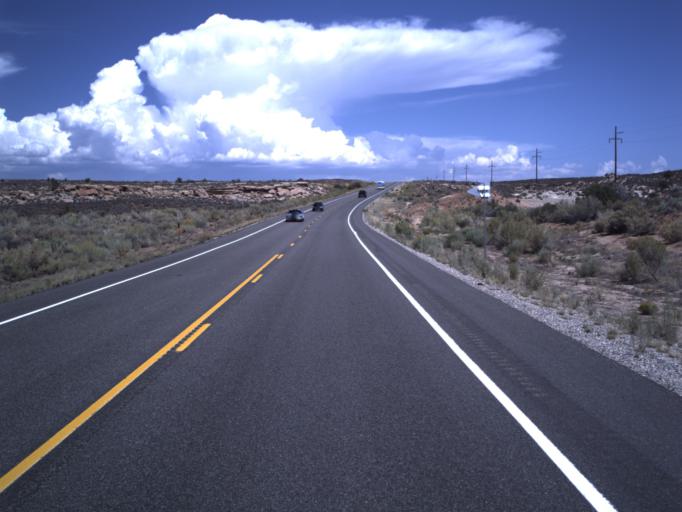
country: US
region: Utah
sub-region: San Juan County
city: Blanding
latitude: 37.3723
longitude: -109.5061
